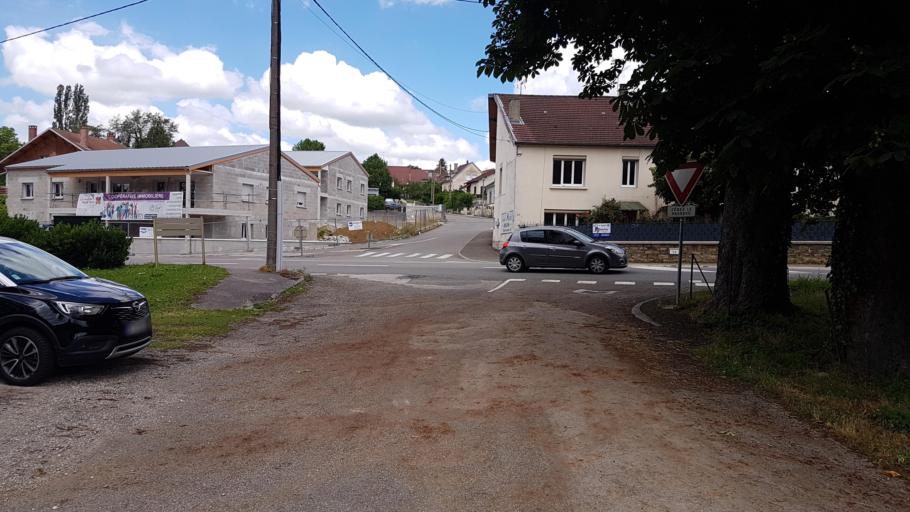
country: FR
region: Franche-Comte
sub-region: Departement du Jura
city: Perrigny
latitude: 46.6653
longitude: 5.5817
